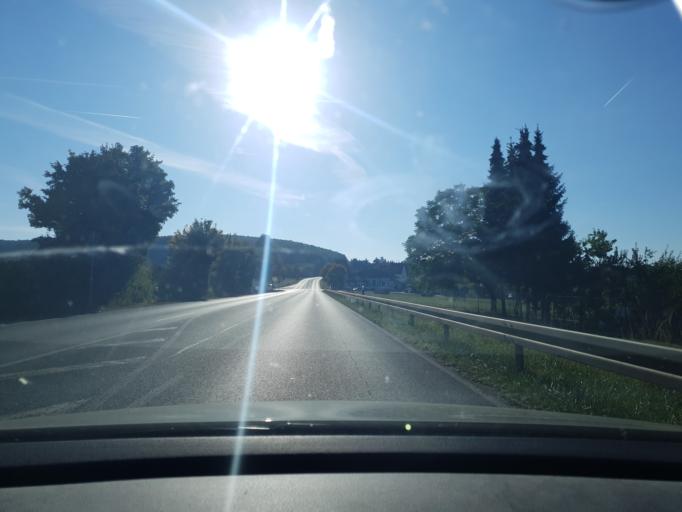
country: DE
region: Hesse
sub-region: Regierungsbezirk Giessen
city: Hoernsheim
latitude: 50.4793
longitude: 8.6156
